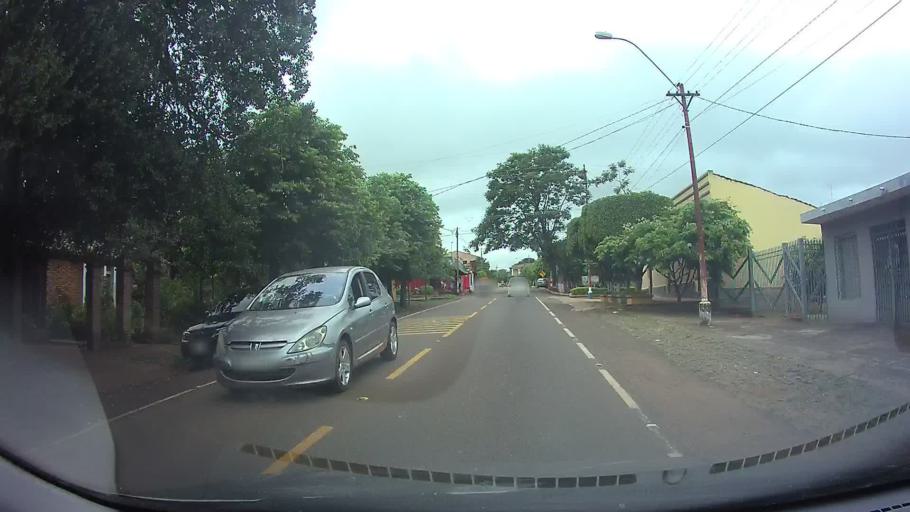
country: PY
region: Paraguari
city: Acahay
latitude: -25.9128
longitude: -57.1150
